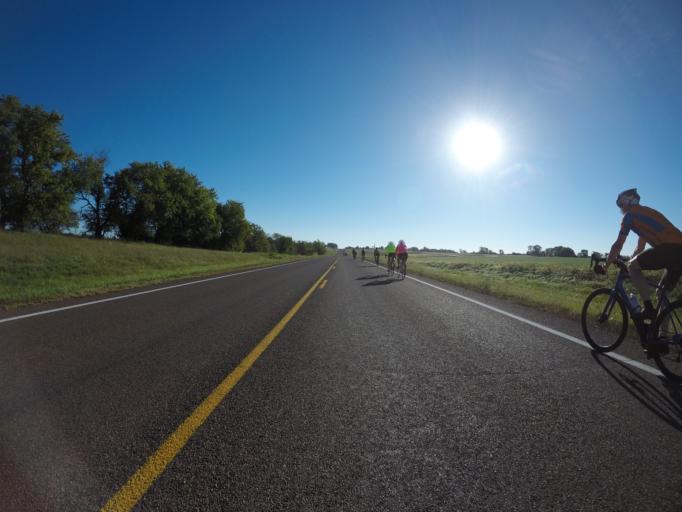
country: US
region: Kansas
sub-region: Douglas County
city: Eudora
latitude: 39.0039
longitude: -95.1071
